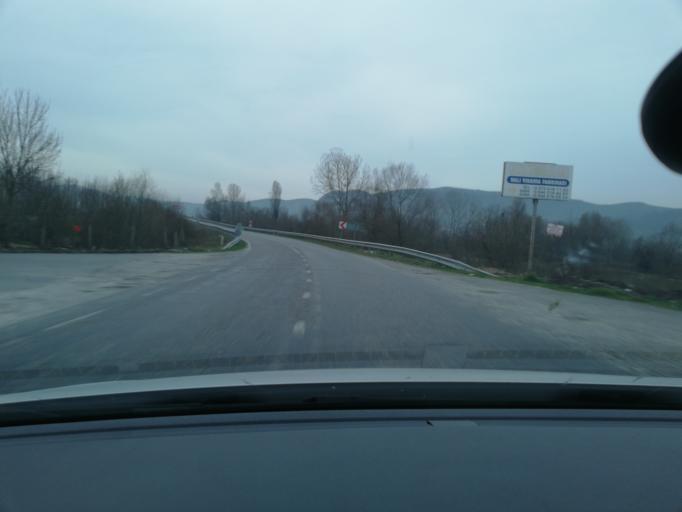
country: TR
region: Zonguldak
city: Saltukova
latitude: 41.5268
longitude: 32.0964
